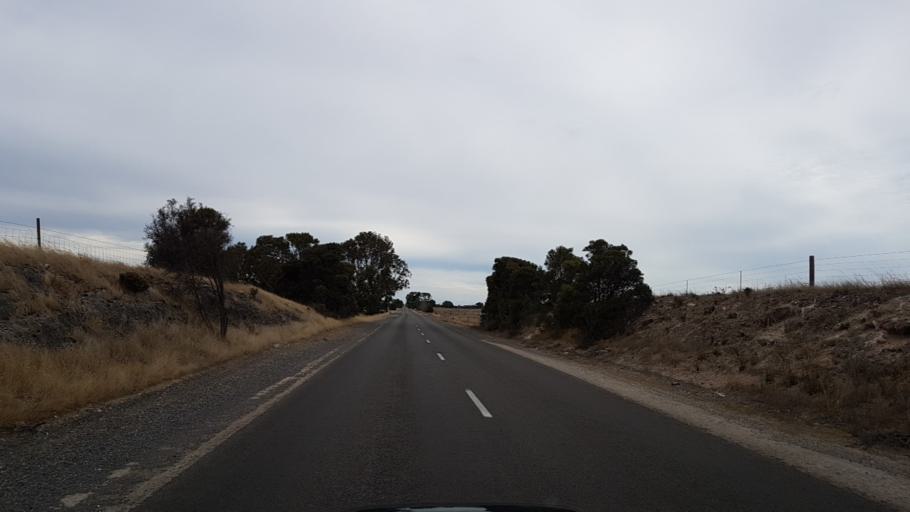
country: AU
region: South Australia
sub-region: Yorke Peninsula
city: Honiton
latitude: -34.9851
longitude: 137.1775
